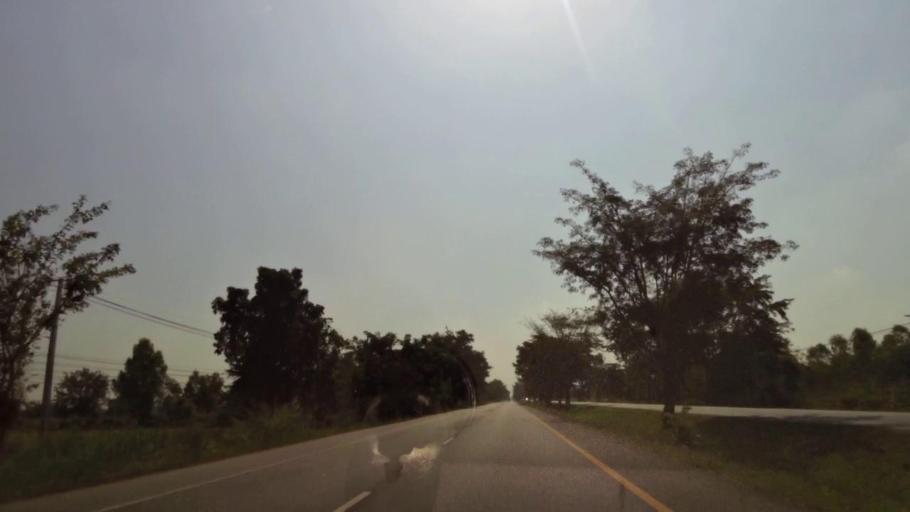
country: TH
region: Phichit
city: Bueng Na Rang
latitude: 16.2864
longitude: 100.1277
